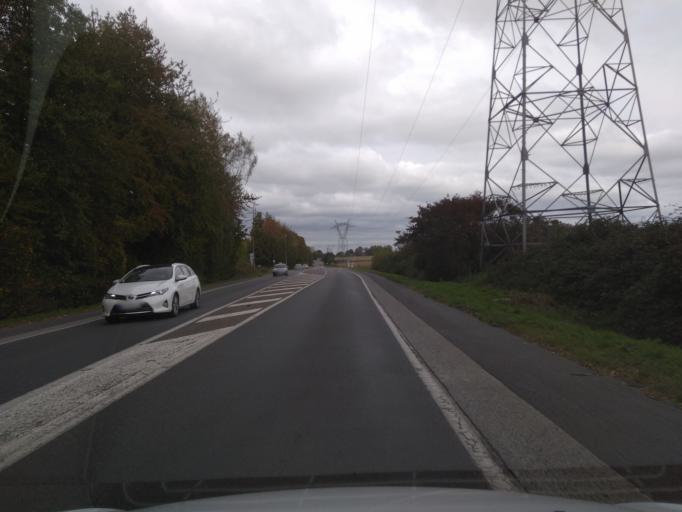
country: FR
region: Nord-Pas-de-Calais
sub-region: Departement du Nord
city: Saint-Saulve
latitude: 50.3658
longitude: 3.5665
